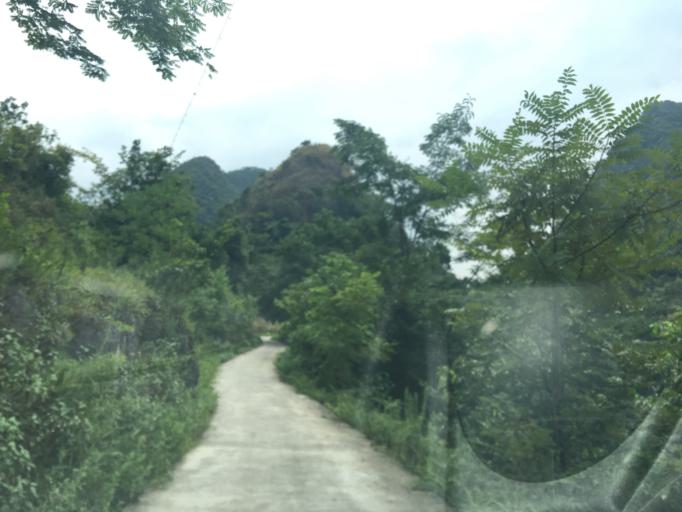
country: CN
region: Guangxi Zhuangzu Zizhiqu
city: Xinzhou
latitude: 25.2342
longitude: 105.6510
